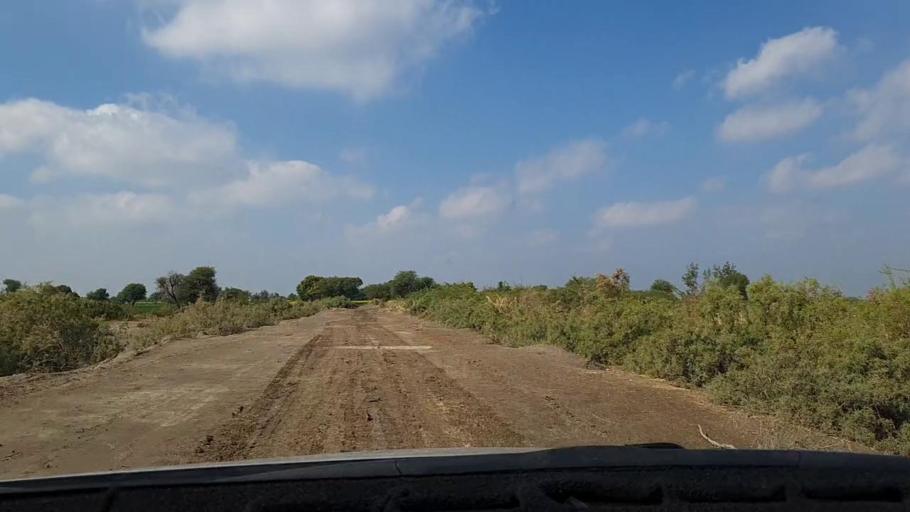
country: PK
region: Sindh
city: Tando Mittha Khan
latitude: 25.7760
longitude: 69.2567
